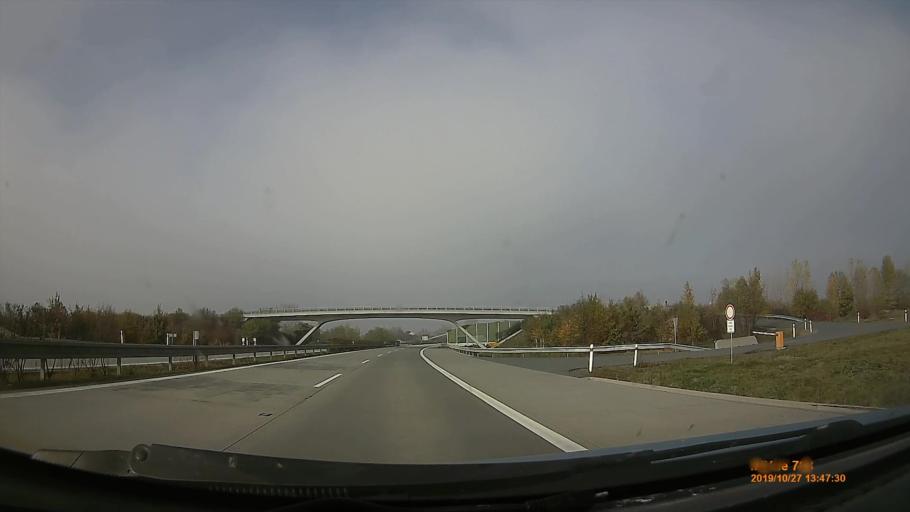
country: CZ
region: Olomoucky
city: Hnevotin
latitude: 49.5882
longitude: 17.2018
